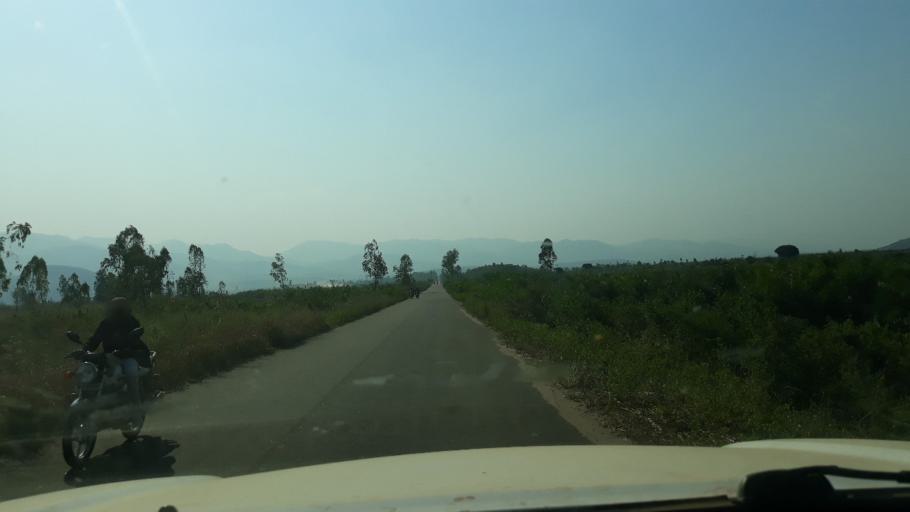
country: BI
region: Cibitoke
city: Cibitoke
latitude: -2.8281
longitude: 29.0122
